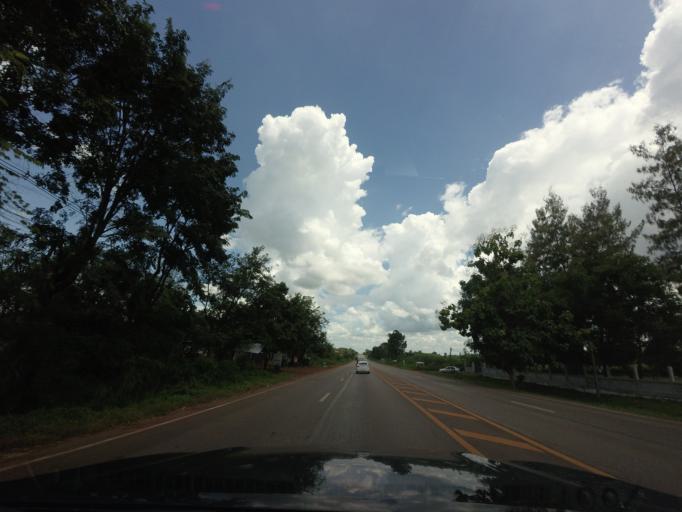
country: TH
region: Changwat Udon Thani
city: Ban Dung
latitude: 17.6858
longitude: 103.2039
